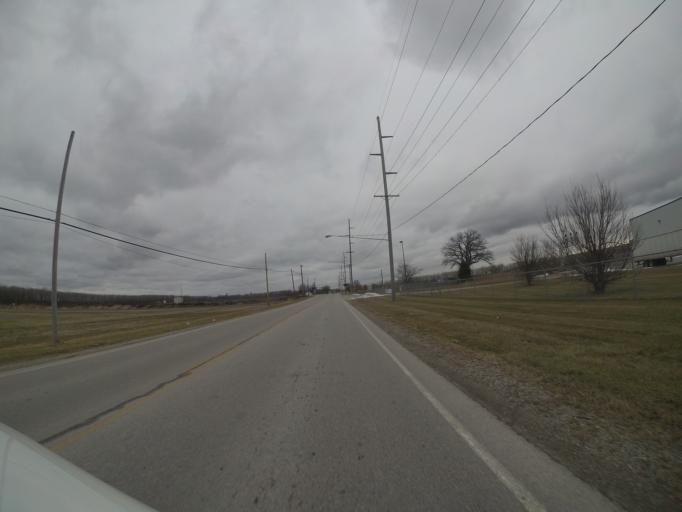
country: US
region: Ohio
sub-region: Wood County
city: Walbridge
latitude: 41.5942
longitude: -83.5127
